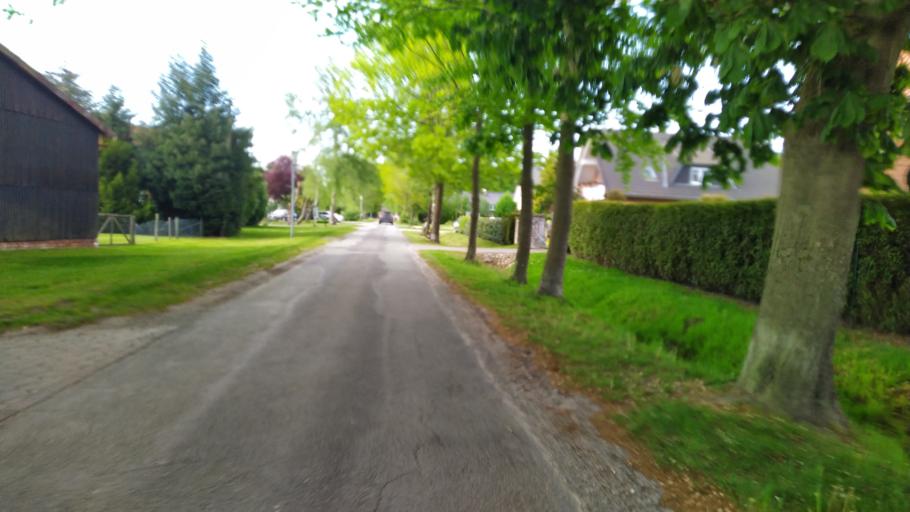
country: DE
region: Lower Saxony
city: Farven
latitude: 53.4301
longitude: 9.3497
